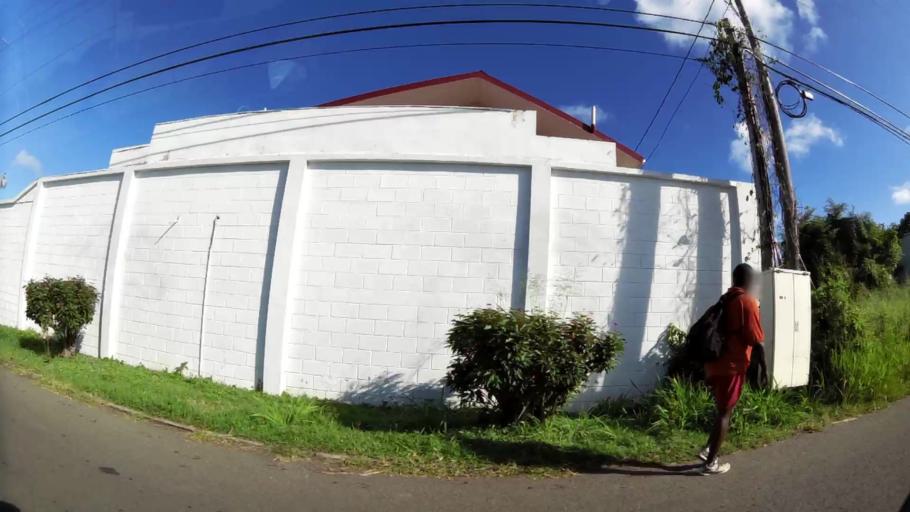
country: TT
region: Tobago
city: Scarborough
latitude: 11.1514
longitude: -60.8444
